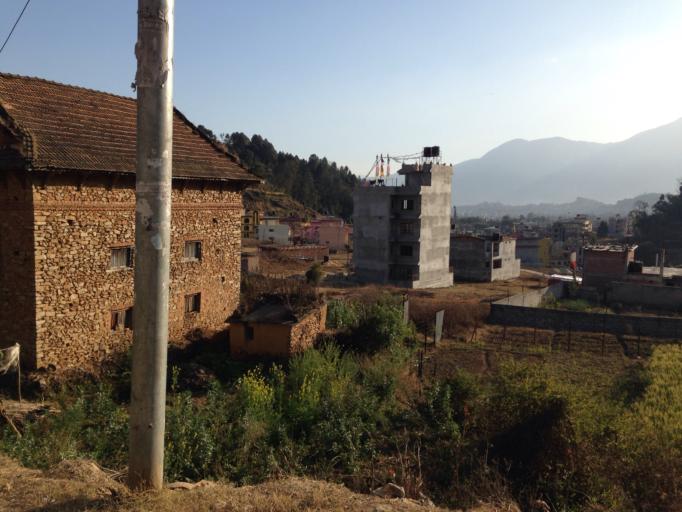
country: NP
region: Central Region
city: Kirtipur
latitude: 27.7242
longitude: 85.2727
